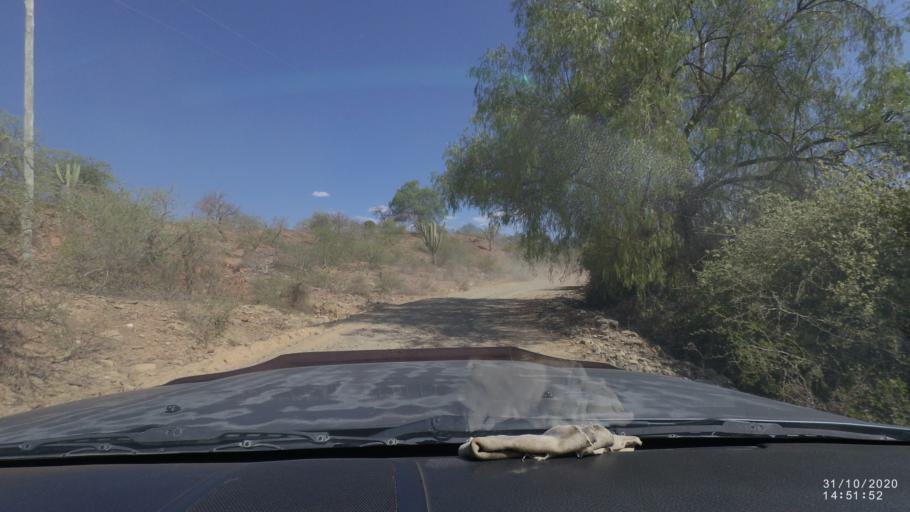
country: BO
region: Cochabamba
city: Aiquile
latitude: -18.2095
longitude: -64.8570
